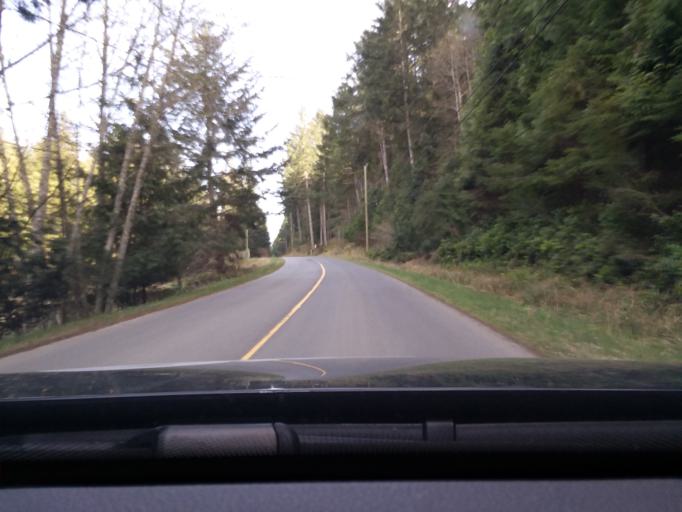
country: CA
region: British Columbia
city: North Saanich
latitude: 48.7518
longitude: -123.2664
